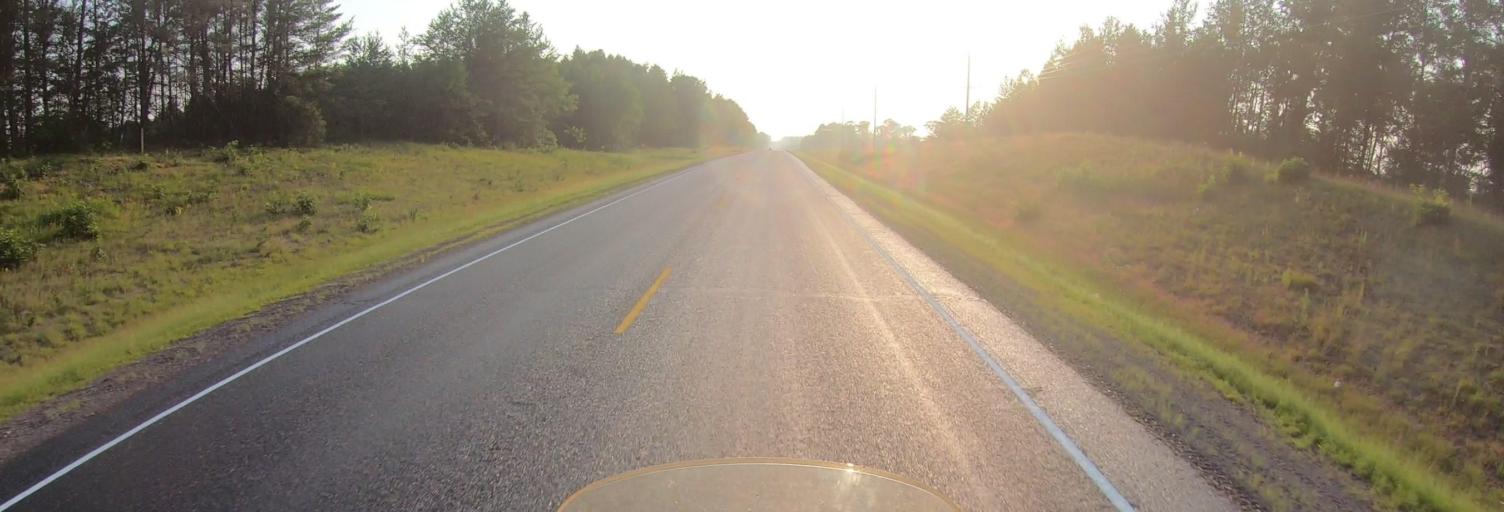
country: US
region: Wisconsin
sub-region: Washburn County
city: Shell Lake
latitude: 45.8154
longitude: -91.9952
